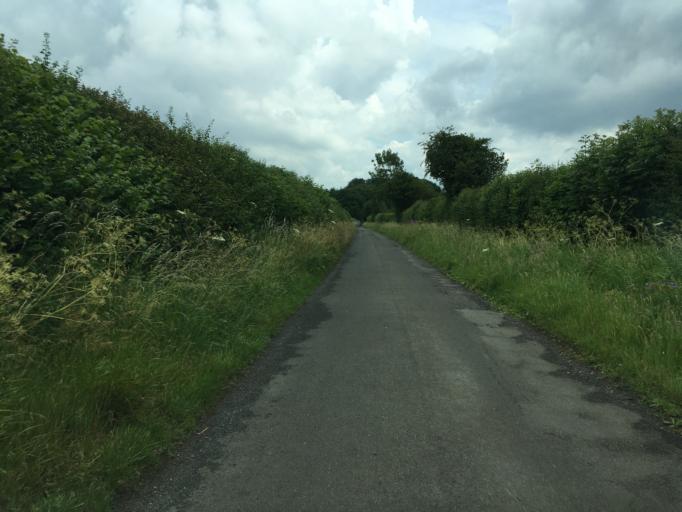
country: GB
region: England
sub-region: Gloucestershire
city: Shurdington
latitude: 51.8069
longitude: -2.0858
